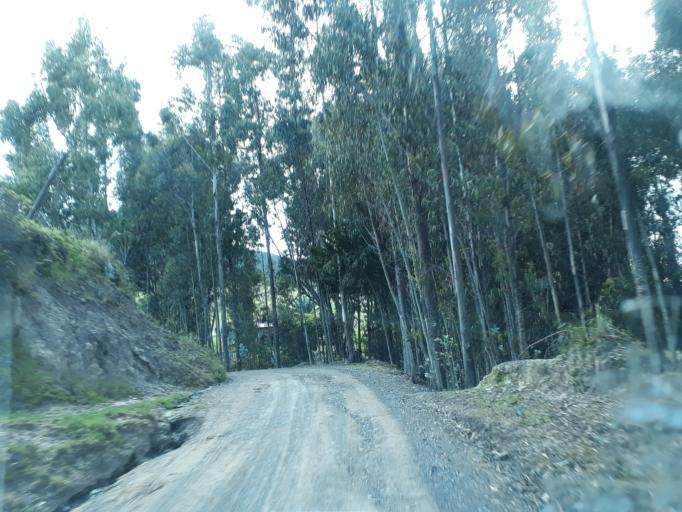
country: CO
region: Cundinamarca
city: Carmen de Carupa
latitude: 5.3160
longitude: -73.9109
